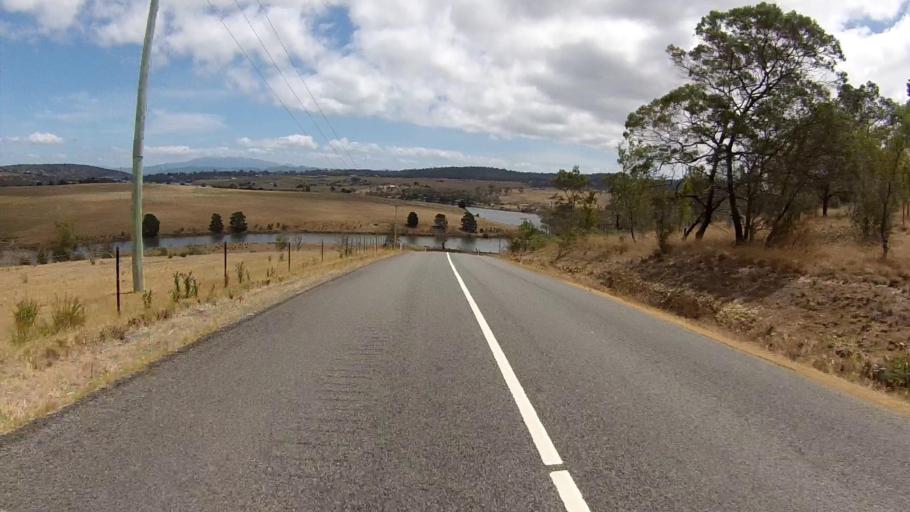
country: AU
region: Tasmania
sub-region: Sorell
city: Sorell
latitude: -42.8673
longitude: 147.6956
